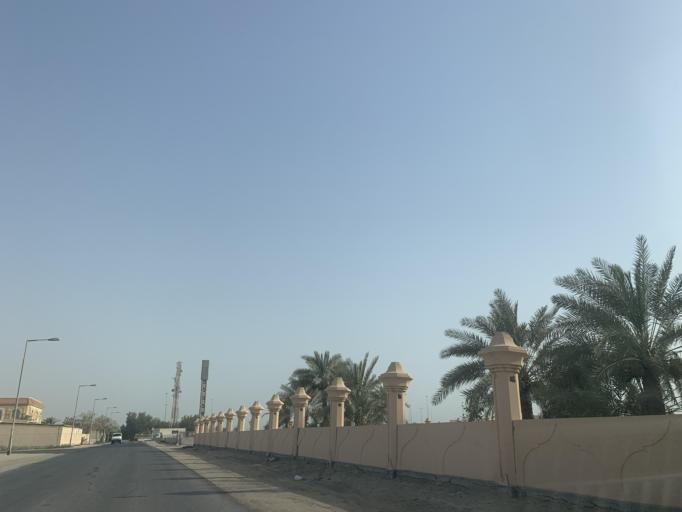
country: BH
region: Central Governorate
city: Madinat Hamad
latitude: 26.1771
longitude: 50.4677
